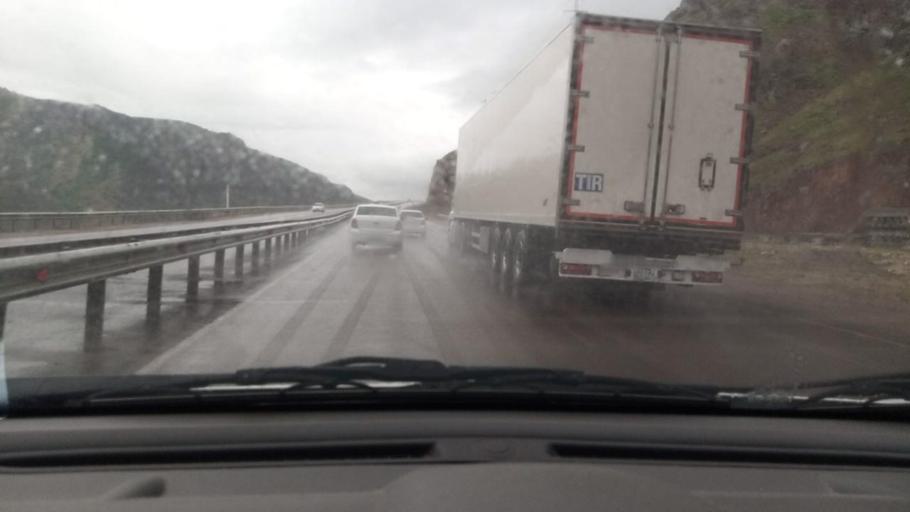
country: UZ
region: Toshkent
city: Angren
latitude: 41.0745
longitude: 70.2847
